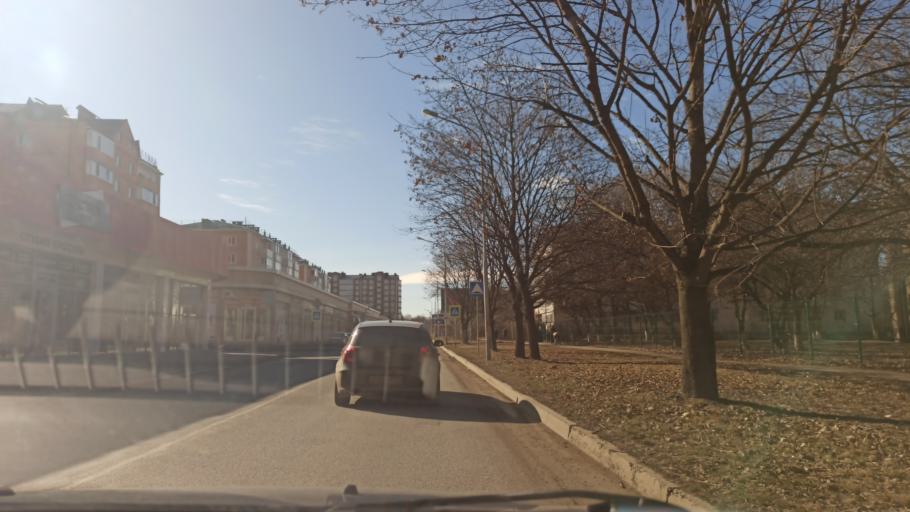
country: RU
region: Stavropol'skiy
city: Yessentukskaya
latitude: 44.0458
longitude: 42.8939
